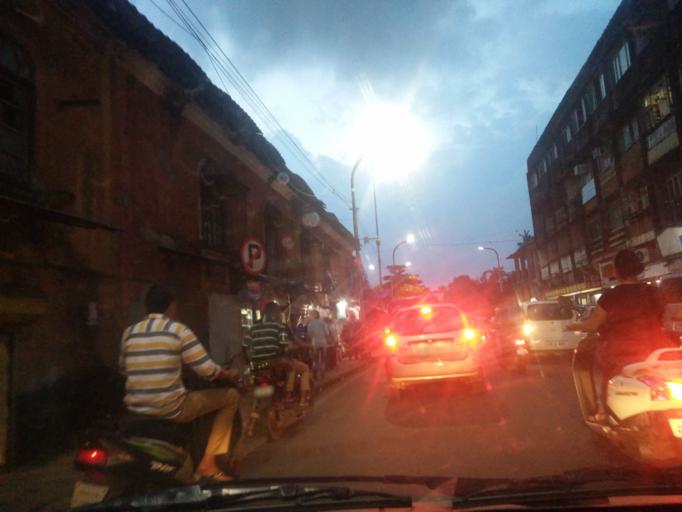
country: IN
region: Goa
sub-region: South Goa
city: Madgaon
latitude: 15.2722
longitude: 73.9595
